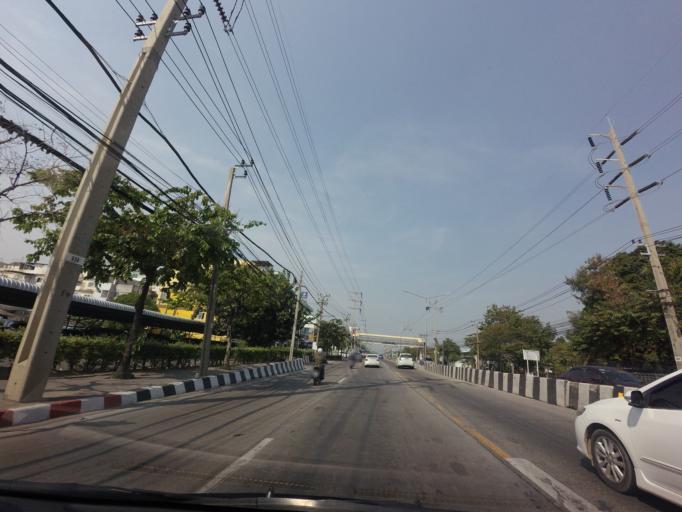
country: TH
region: Bangkok
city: Lat Krabang
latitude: 13.7477
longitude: 100.7465
